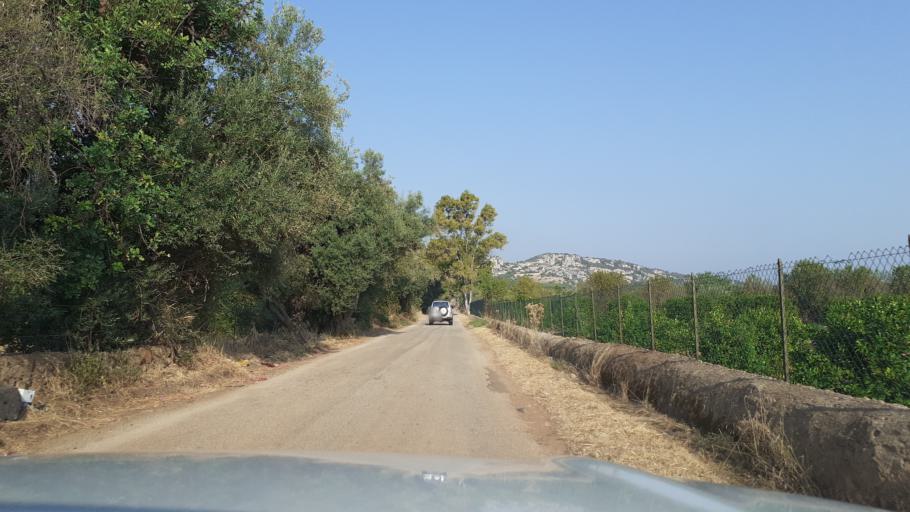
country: IT
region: Sicily
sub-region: Provincia di Siracusa
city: Cassibile
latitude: 36.9748
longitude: 15.1871
